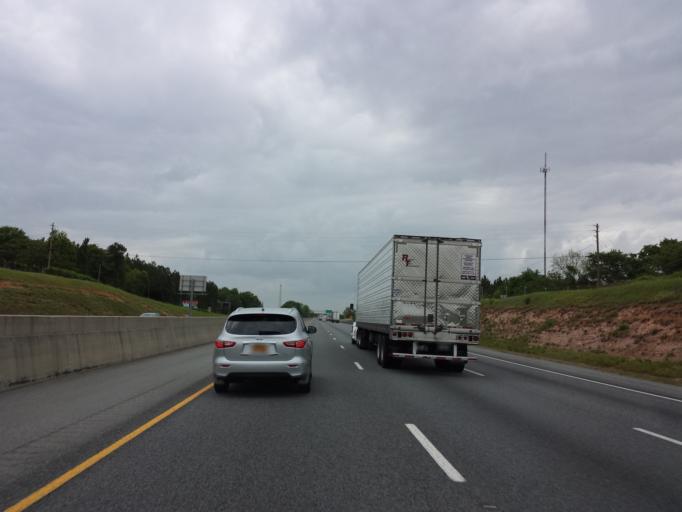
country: US
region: Georgia
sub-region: Tift County
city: Tifton
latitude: 31.5639
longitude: -83.5427
